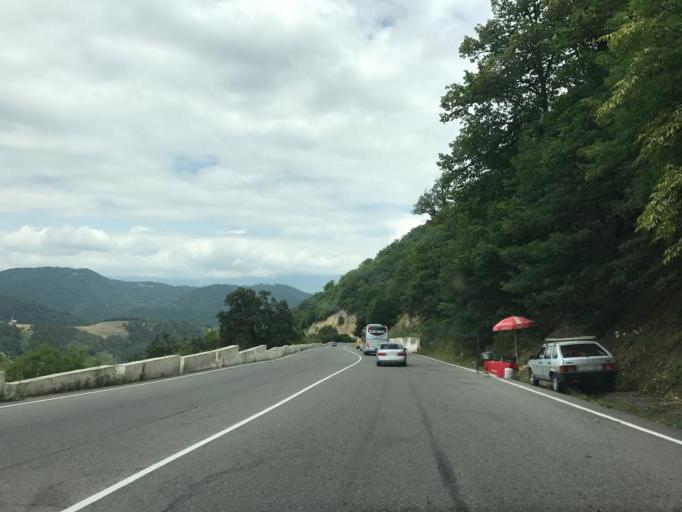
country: AM
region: Tavush
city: Dilijan
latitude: 40.6903
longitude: 44.8603
